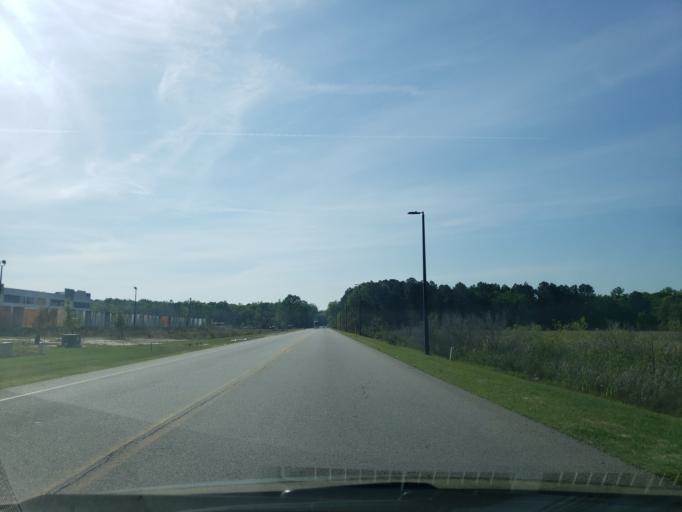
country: US
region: Georgia
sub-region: Chatham County
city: Garden City
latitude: 32.1022
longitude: -81.1871
